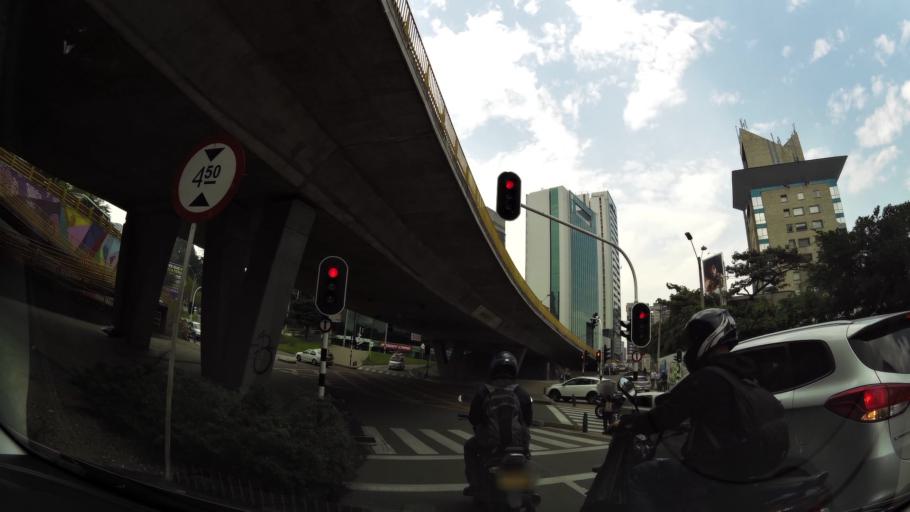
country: CO
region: Antioquia
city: Envigado
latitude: 6.1963
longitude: -75.5750
